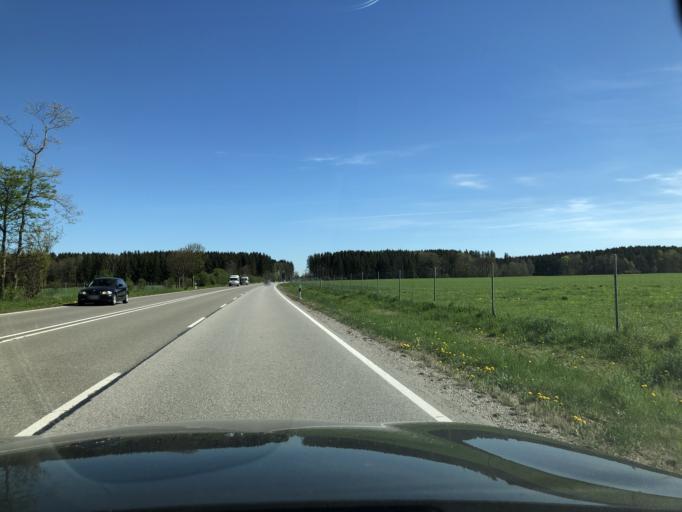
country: DE
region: Bavaria
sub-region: Swabia
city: Jengen
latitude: 47.9769
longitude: 10.6905
